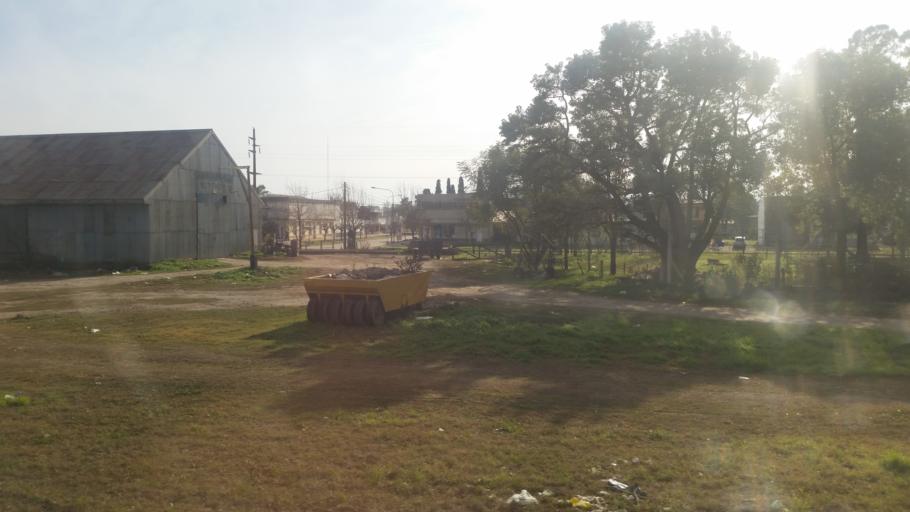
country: AR
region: Cordoba
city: Morrison
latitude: -32.5953
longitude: -62.8342
